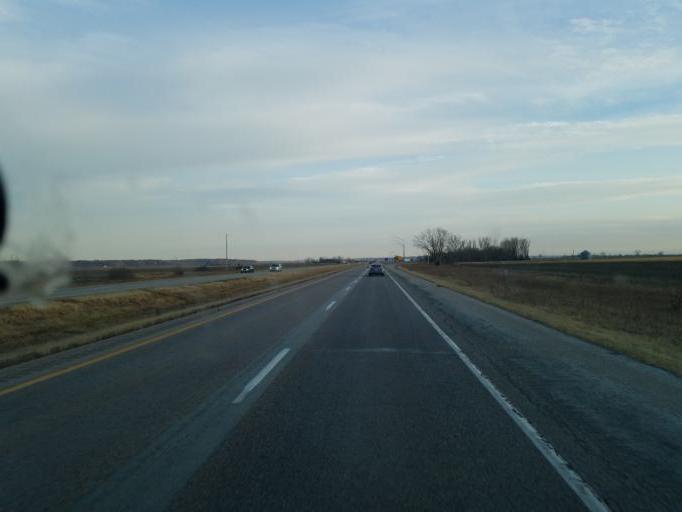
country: US
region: Iowa
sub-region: Harrison County
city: Missouri Valley
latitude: 41.5961
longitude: -95.9577
